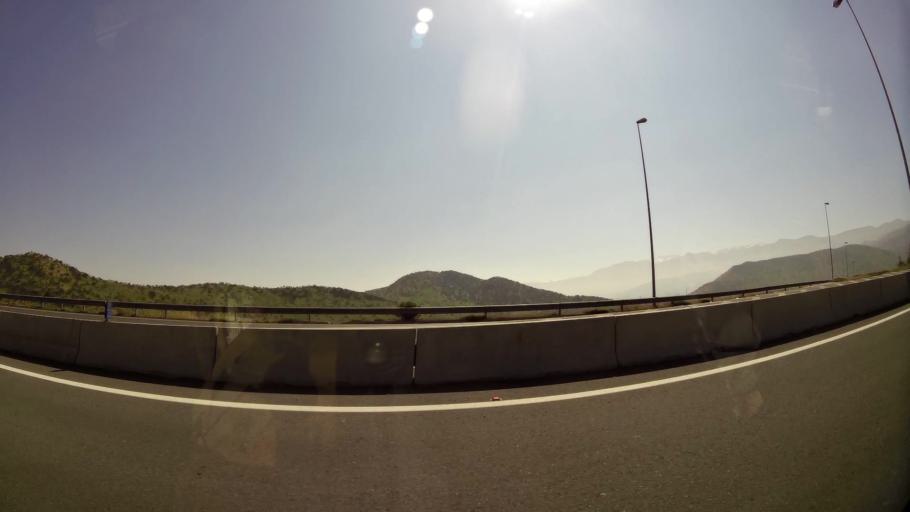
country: CL
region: Santiago Metropolitan
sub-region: Provincia de Chacabuco
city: Chicureo Abajo
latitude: -33.2999
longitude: -70.6622
